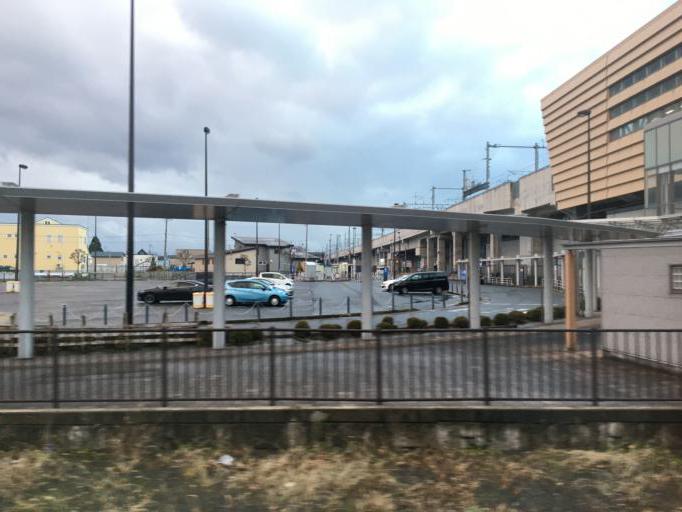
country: JP
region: Aomori
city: Aomori Shi
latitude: 40.8274
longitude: 140.6940
